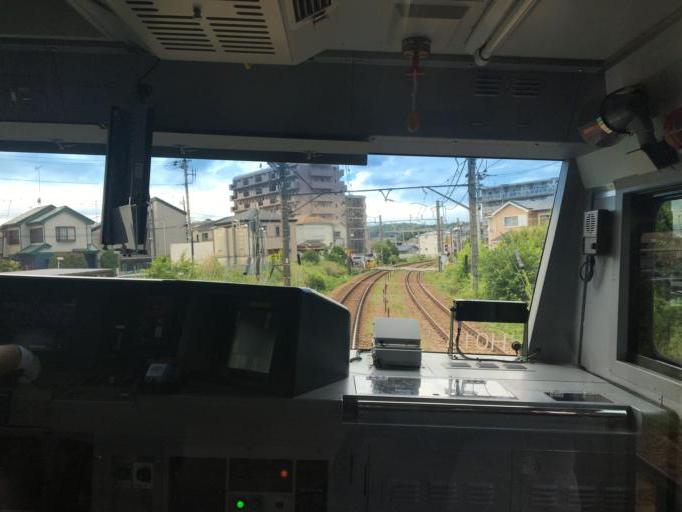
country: JP
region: Tokyo
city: Hachioji
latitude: 35.6008
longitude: 139.3340
